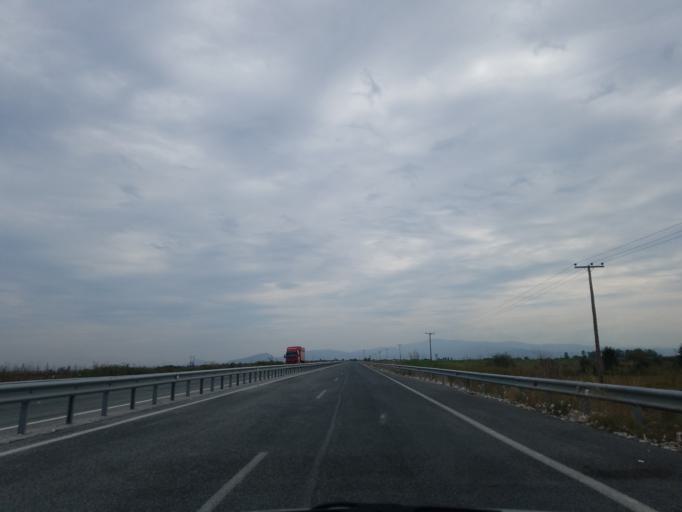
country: GR
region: Thessaly
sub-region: Nomos Kardhitsas
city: Sofades
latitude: 39.2943
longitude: 22.1669
